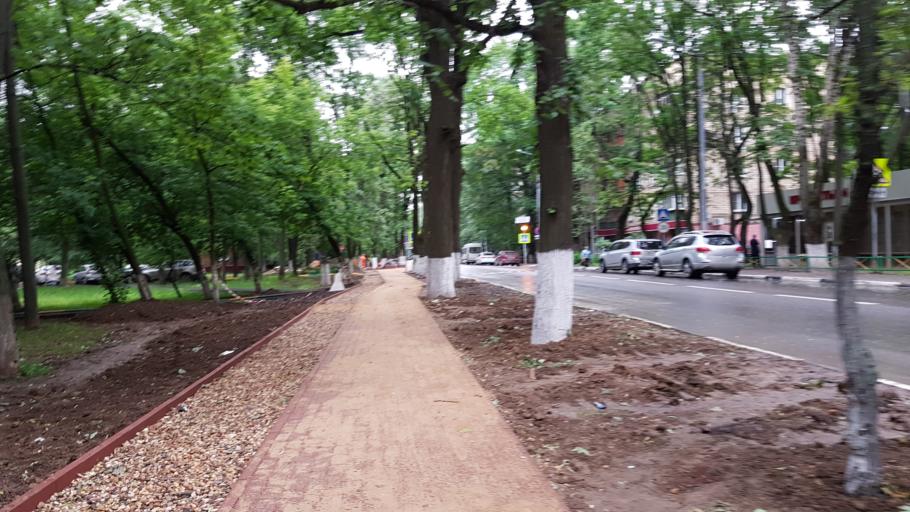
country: RU
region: Moscow
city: Khimki
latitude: 55.8909
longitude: 37.4518
